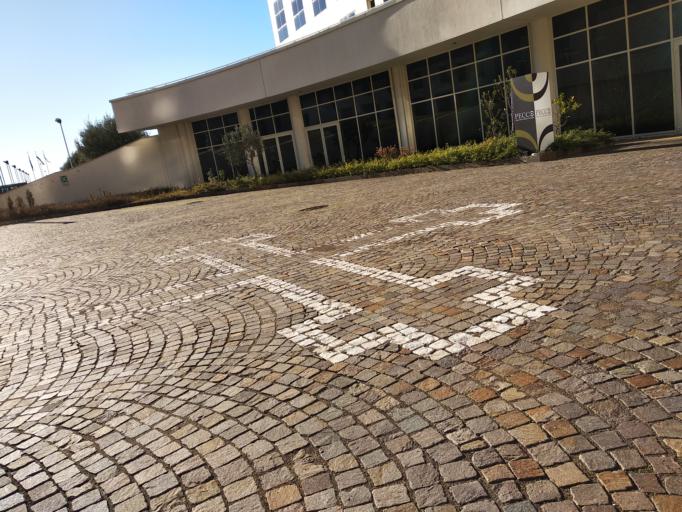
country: IT
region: Calabria
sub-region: Provincia di Catanzaro
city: Catanzaro
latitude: 38.8604
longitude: 16.5721
